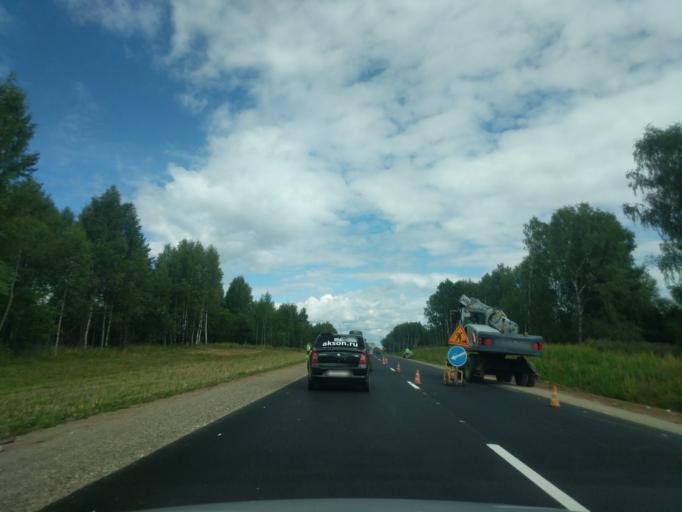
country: RU
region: Kostroma
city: Kosmynino
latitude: 57.7214
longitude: 40.7834
